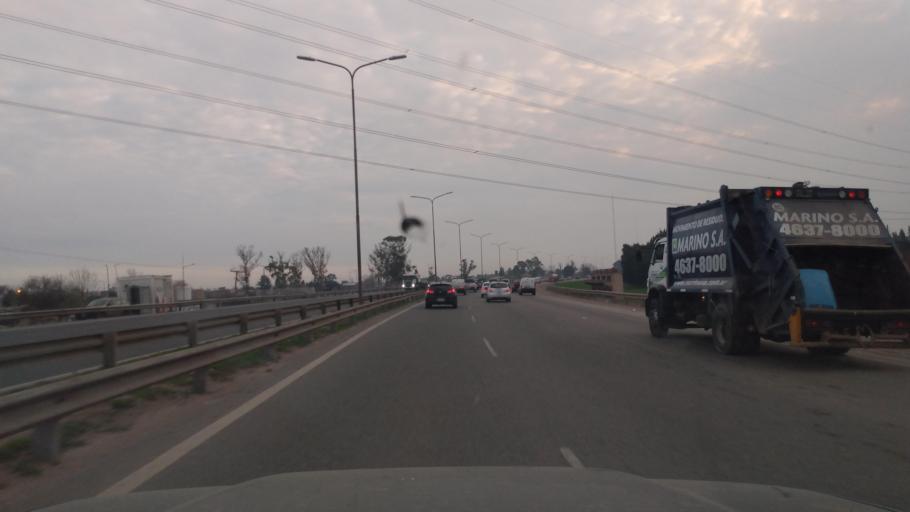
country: AR
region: Buenos Aires
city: Hurlingham
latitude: -34.5499
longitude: -58.6074
